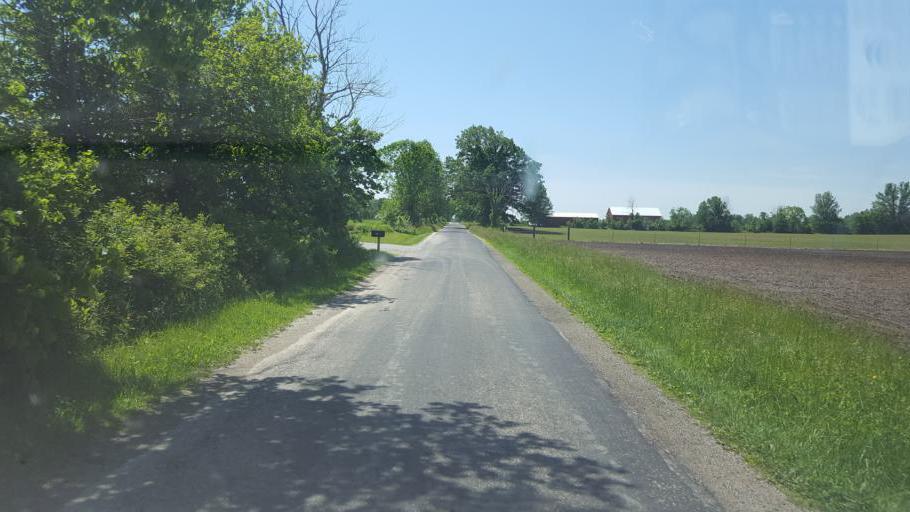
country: US
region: Ohio
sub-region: Union County
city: Richwood
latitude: 40.5906
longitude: -83.4102
